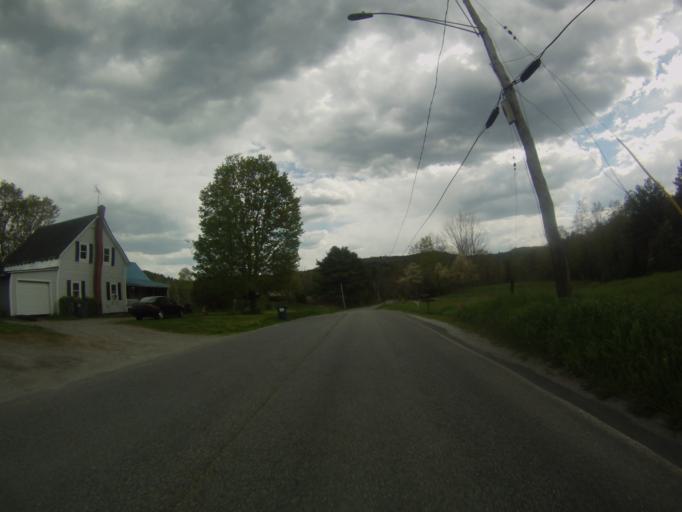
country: US
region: New York
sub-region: Essex County
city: Mineville
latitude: 44.0495
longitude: -73.5546
